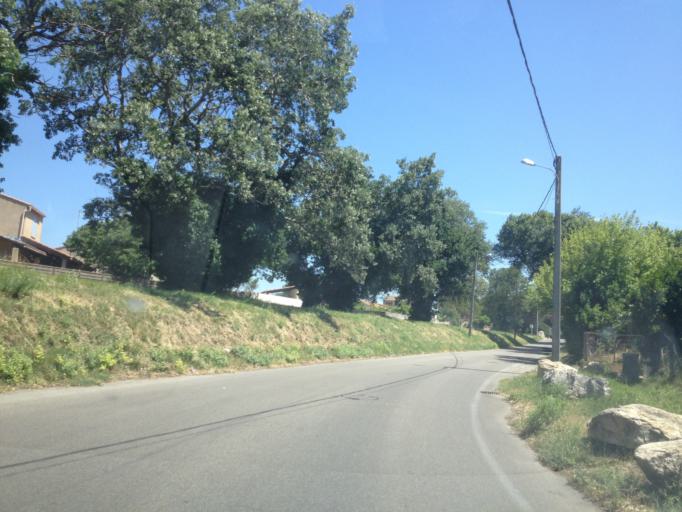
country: FR
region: Provence-Alpes-Cote d'Azur
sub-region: Departement du Vaucluse
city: Sorgues
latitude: 44.0169
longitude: 4.8753
